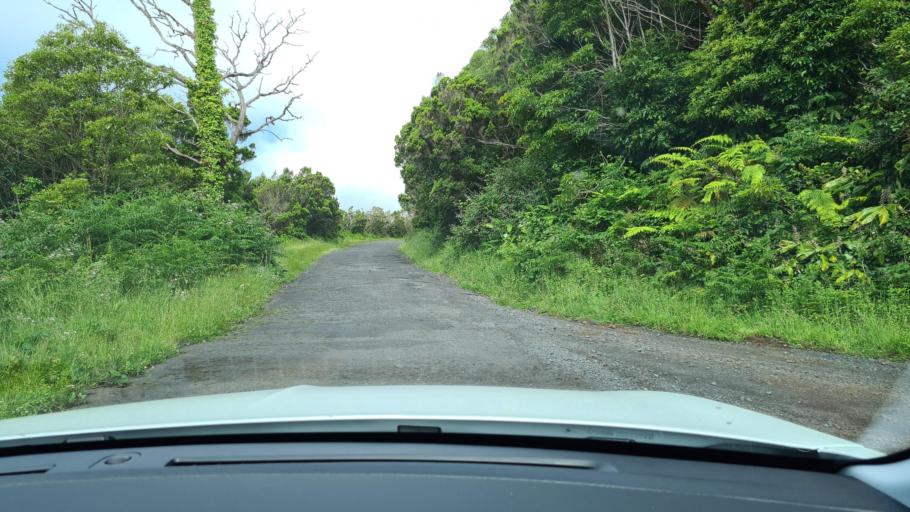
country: PT
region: Azores
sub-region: Sao Roque do Pico
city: Sao Roque do Pico
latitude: 38.6604
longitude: -28.1214
